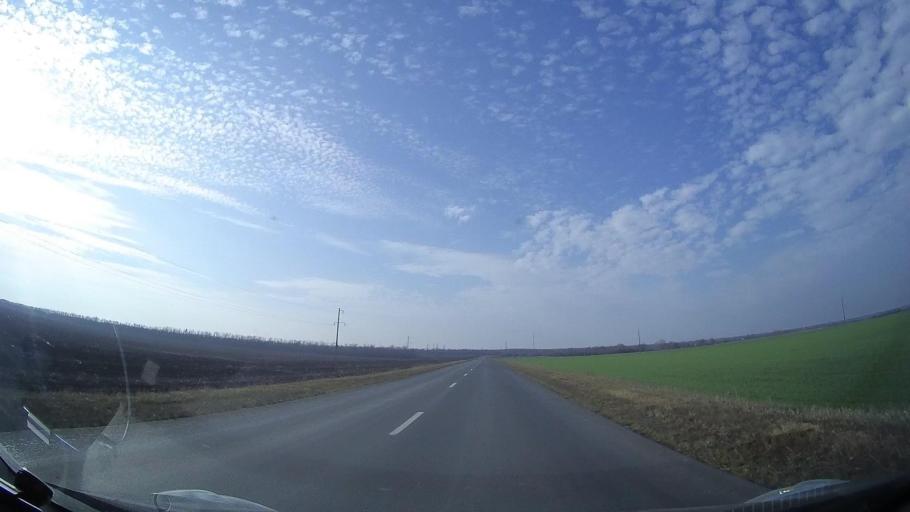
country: RU
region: Rostov
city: Veselyy
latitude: 46.9689
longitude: 40.6408
